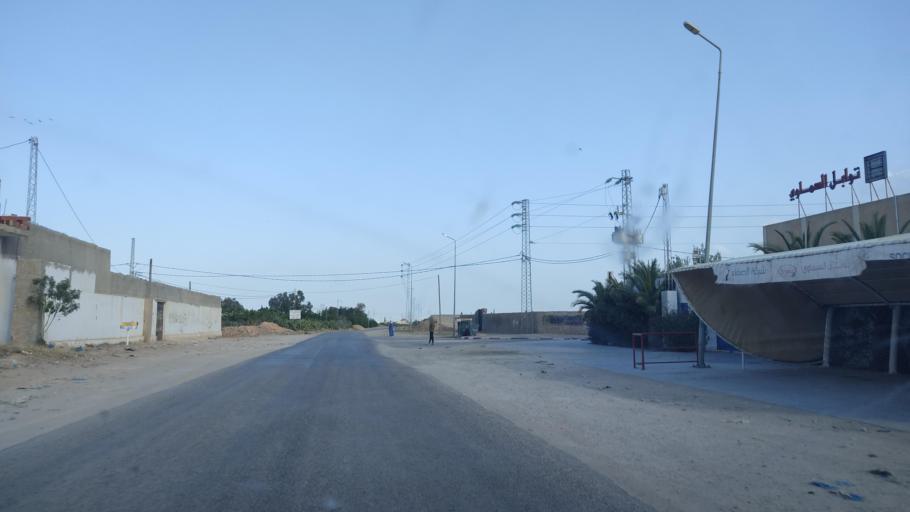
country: TN
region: Safaqis
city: Sfax
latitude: 34.8097
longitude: 10.6638
